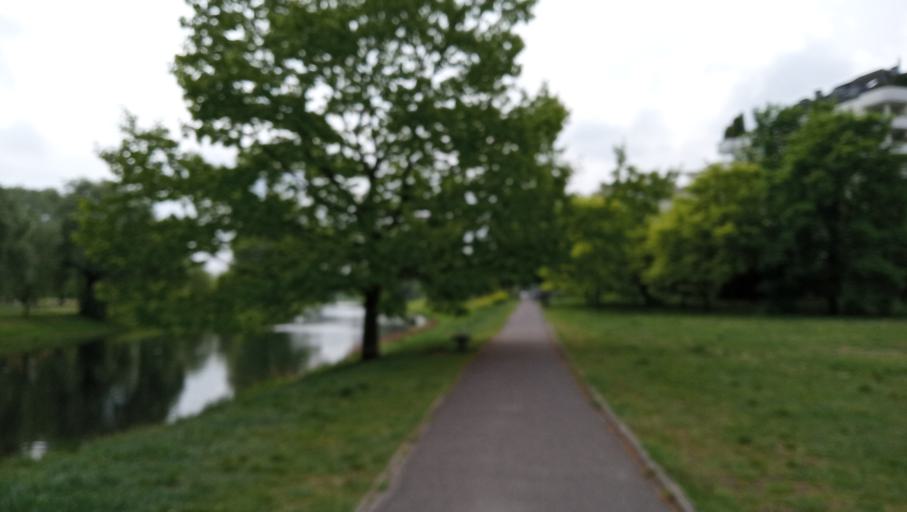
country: PL
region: Masovian Voivodeship
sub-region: Warszawa
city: Zoliborz
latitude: 52.2791
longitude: 20.9892
